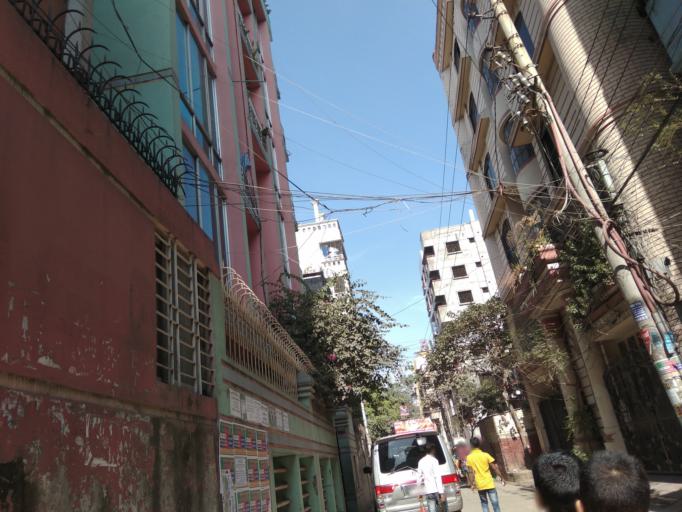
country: BD
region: Dhaka
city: Azimpur
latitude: 23.7737
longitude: 90.3593
